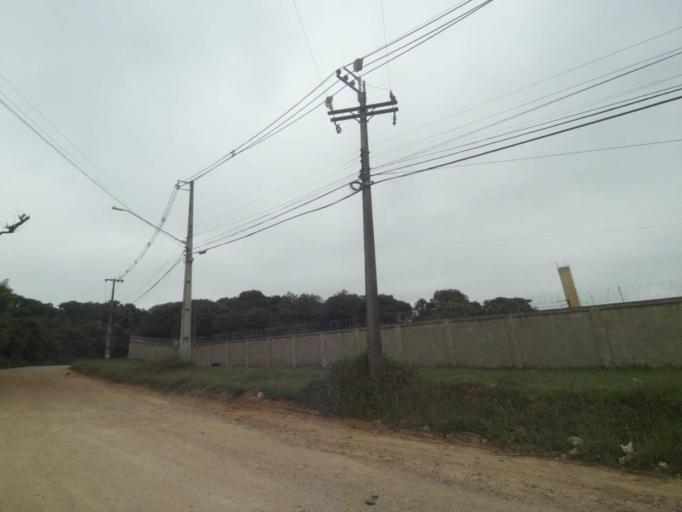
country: BR
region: Parana
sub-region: Araucaria
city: Araucaria
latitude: -25.5165
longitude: -49.3513
